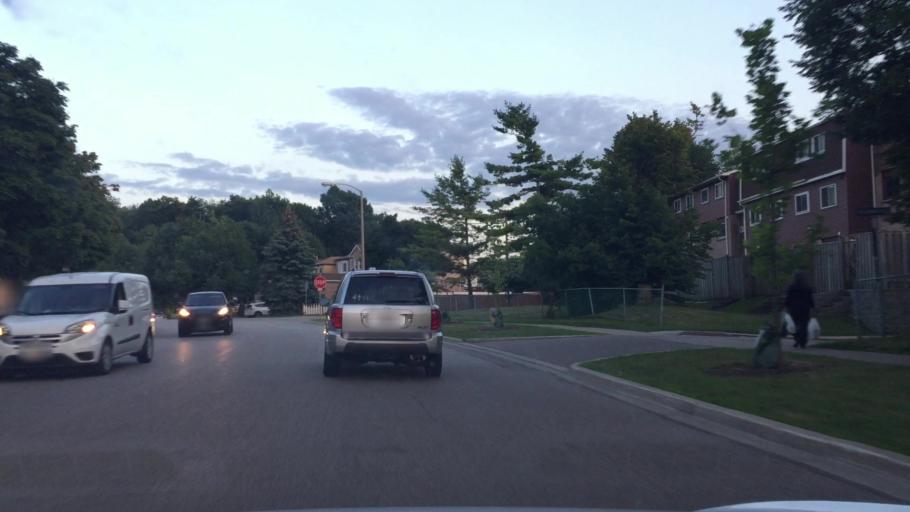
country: CA
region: Ontario
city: Scarborough
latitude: 43.8002
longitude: -79.2067
